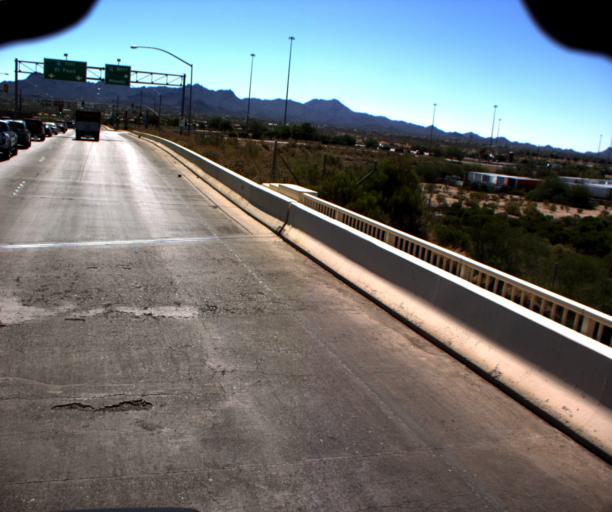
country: US
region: Arizona
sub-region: Pima County
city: Flowing Wells
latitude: 32.2608
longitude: -111.0005
